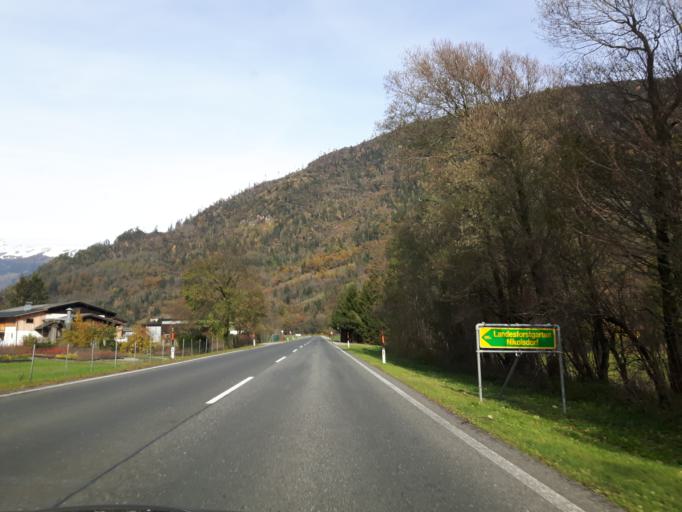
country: AT
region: Tyrol
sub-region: Politischer Bezirk Lienz
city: Lavant
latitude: 46.7954
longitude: 12.8747
